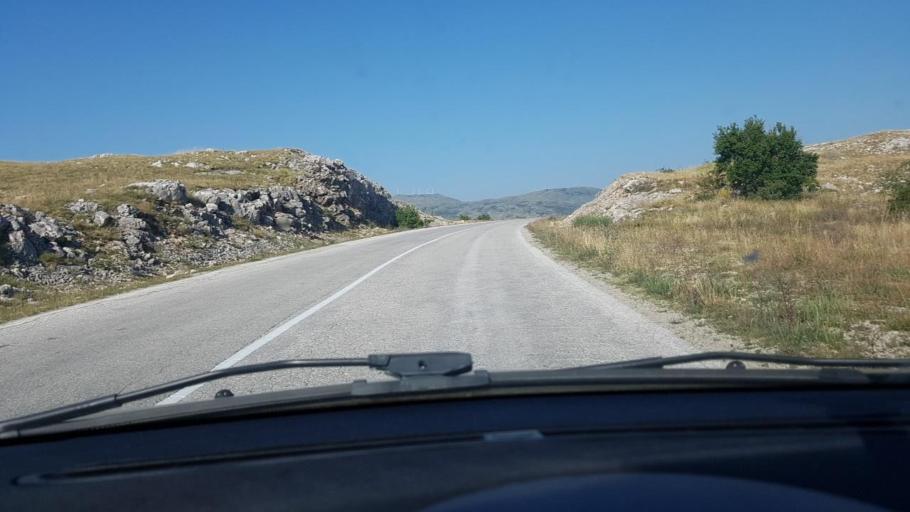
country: BA
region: Federation of Bosnia and Herzegovina
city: Tomislavgrad
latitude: 43.7882
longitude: 17.2493
